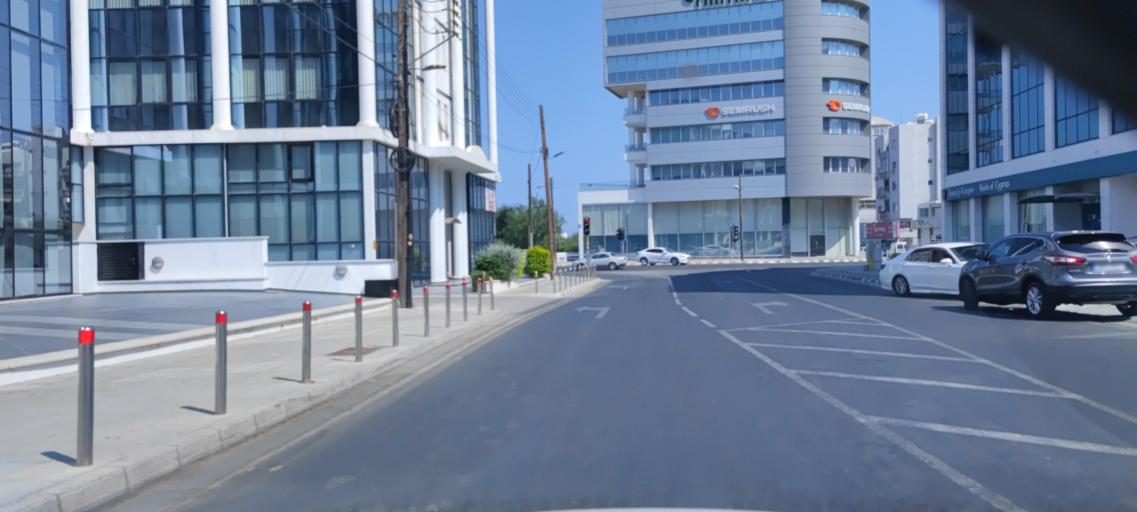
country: CY
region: Limassol
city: Limassol
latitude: 34.6947
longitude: 33.0651
